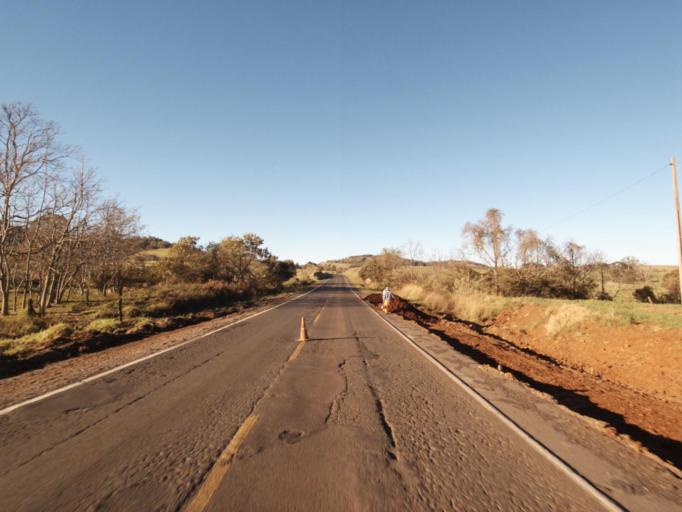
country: AR
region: Misiones
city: Bernardo de Irigoyen
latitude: -26.3654
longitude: -53.5342
